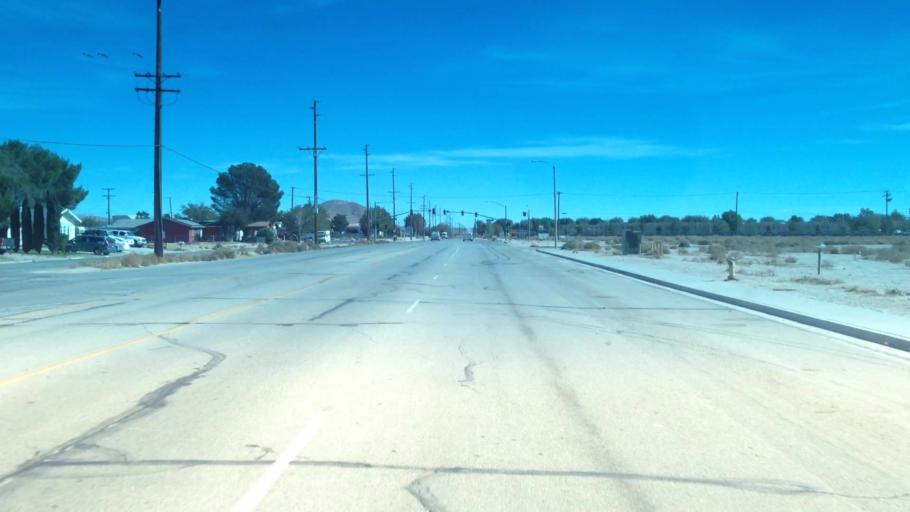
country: US
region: California
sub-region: Kern County
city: Rosamond
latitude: 34.8644
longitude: -118.1610
